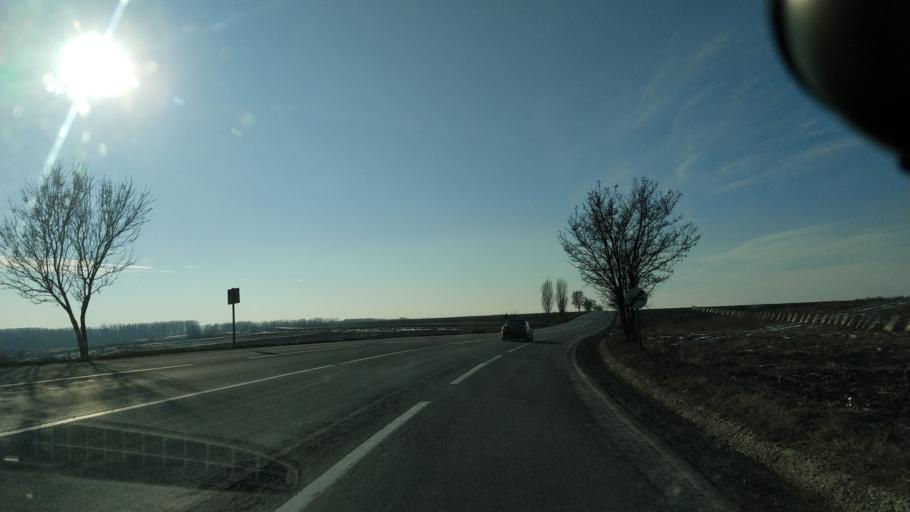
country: RO
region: Iasi
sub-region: Comuna Butea
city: Butea
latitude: 47.0917
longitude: 26.9187
